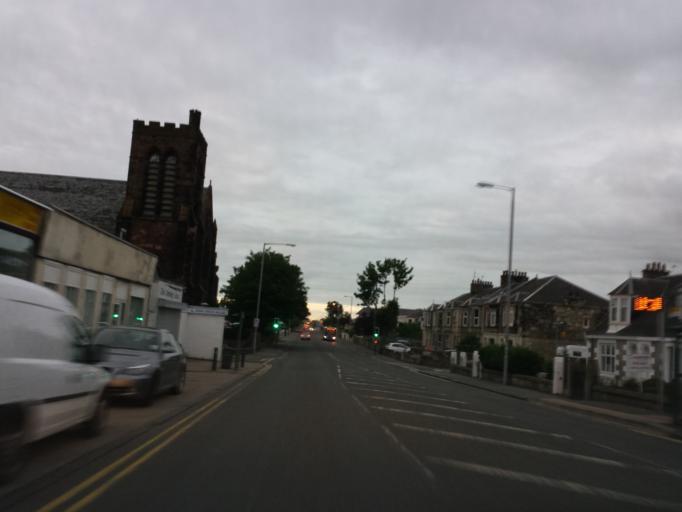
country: GB
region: Scotland
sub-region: South Ayrshire
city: Prestwick
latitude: 55.4734
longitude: -4.6249
